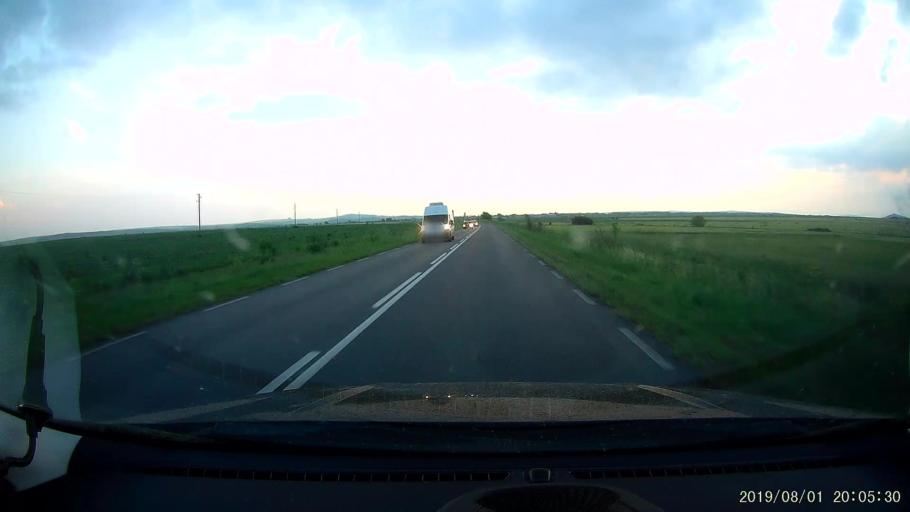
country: BG
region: Yambol
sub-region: Obshtina Yambol
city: Yambol
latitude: 42.5454
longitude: 26.5659
